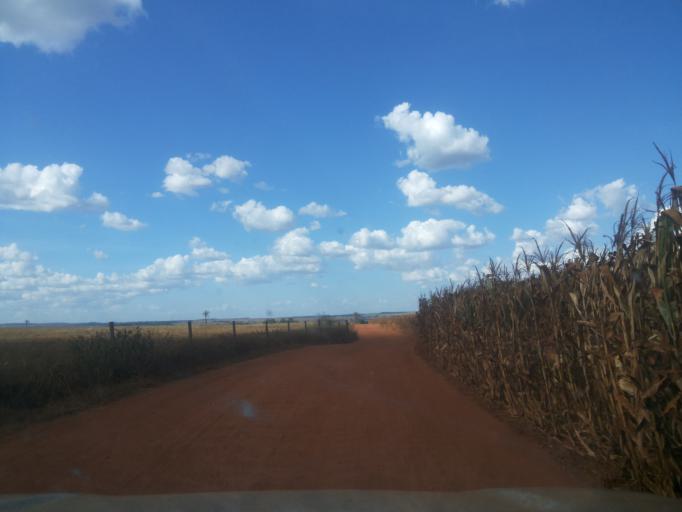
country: BR
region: Minas Gerais
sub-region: Capinopolis
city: Capinopolis
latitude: -18.5827
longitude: -49.5037
